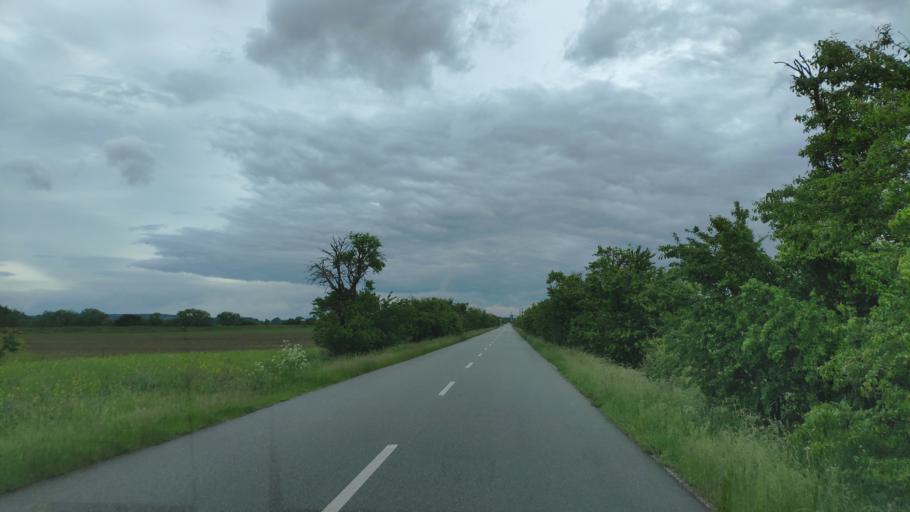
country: SK
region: Kosicky
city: Moldava nad Bodvou
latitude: 48.5840
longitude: 21.1379
